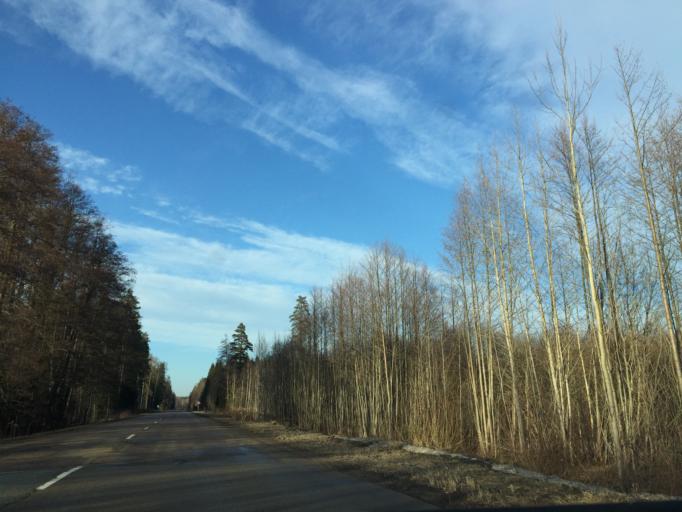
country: LV
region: Kekava
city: Balozi
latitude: 56.7387
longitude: 24.1088
